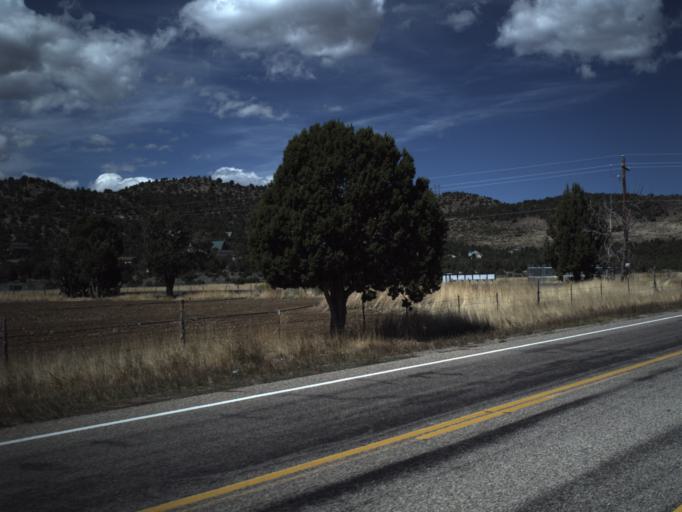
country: US
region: Utah
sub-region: Washington County
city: Enterprise
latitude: 37.4164
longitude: -113.6321
